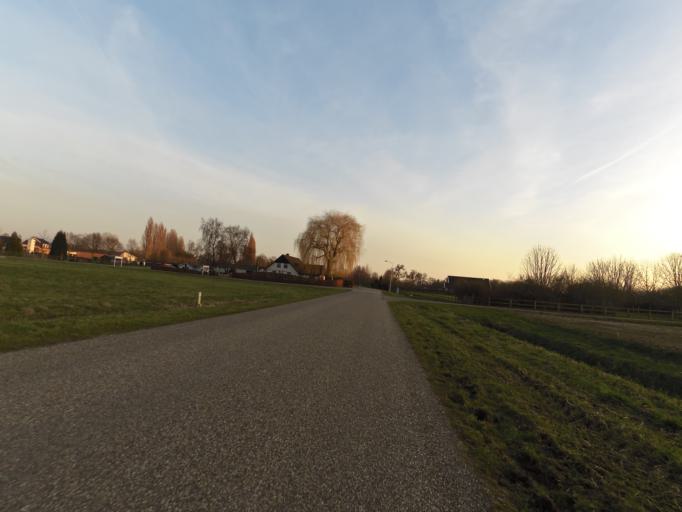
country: NL
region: Gelderland
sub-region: Gemeente Zevenaar
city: Zevenaar
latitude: 51.9459
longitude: 6.1149
